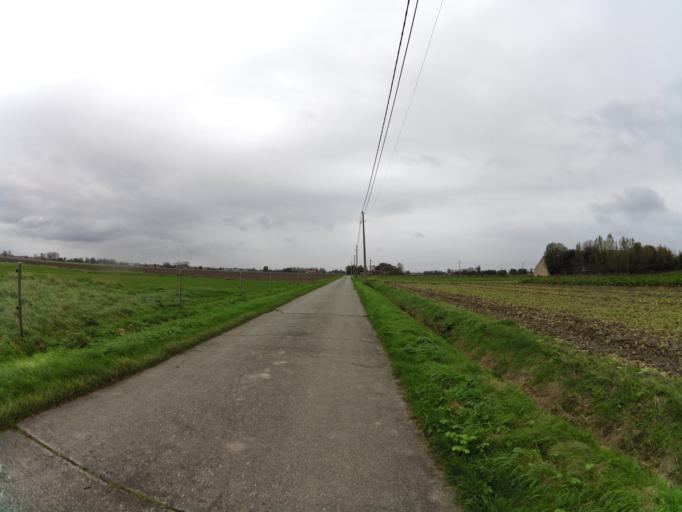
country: BE
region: Flanders
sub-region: Provincie West-Vlaanderen
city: Gistel
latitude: 51.1235
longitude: 2.9295
